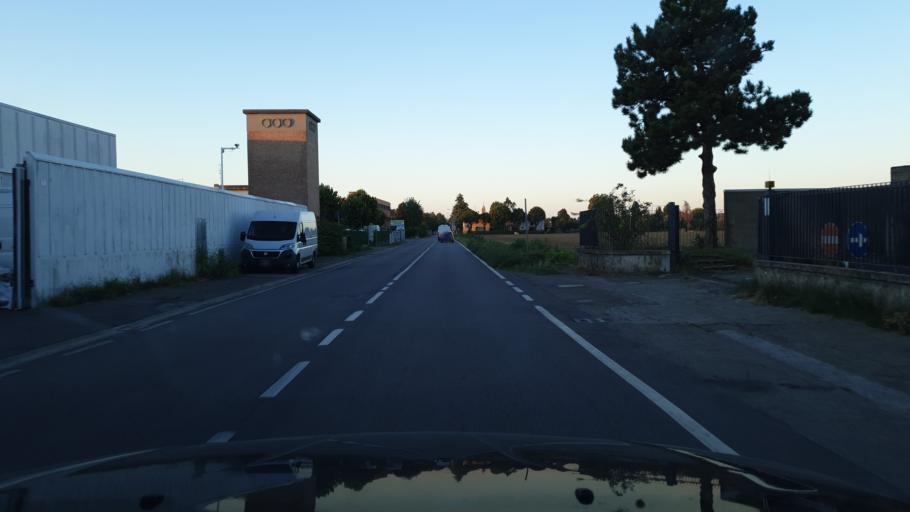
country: IT
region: Emilia-Romagna
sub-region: Provincia di Bologna
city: Quarto Inferiore
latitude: 44.5434
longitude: 11.3956
